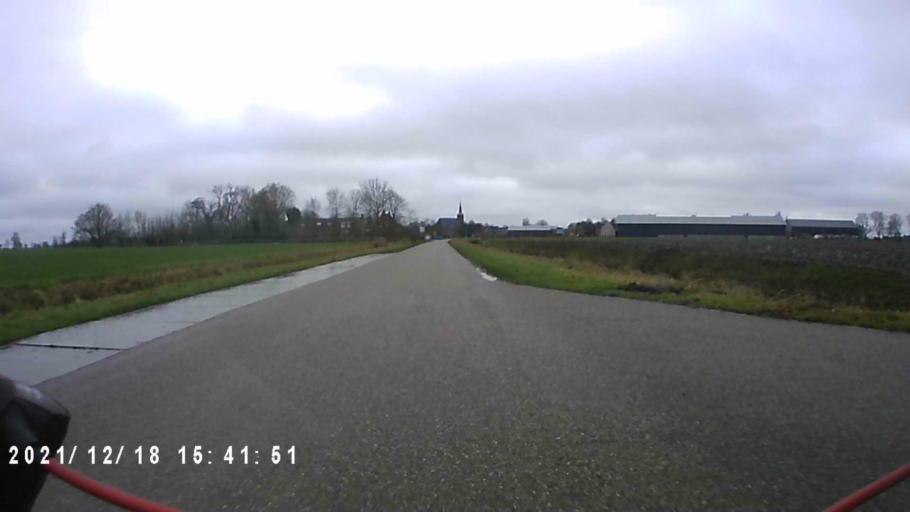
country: NL
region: Friesland
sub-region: Gemeente Dongeradeel
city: Anjum
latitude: 53.3346
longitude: 6.1058
